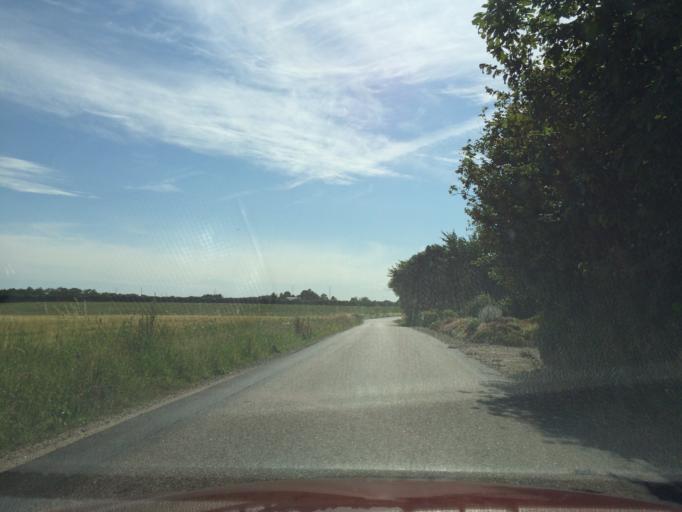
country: DK
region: Central Jutland
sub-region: Silkeborg Kommune
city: Silkeborg
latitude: 56.2234
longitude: 9.5801
